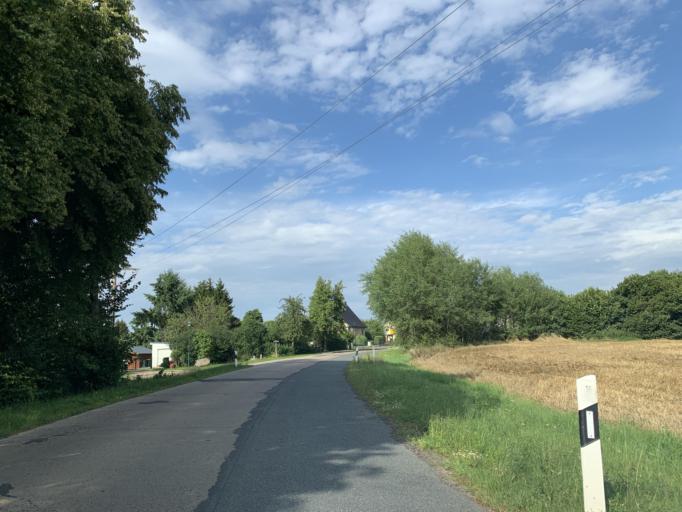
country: DE
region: Mecklenburg-Vorpommern
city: Carpin
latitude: 53.3741
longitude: 13.1782
